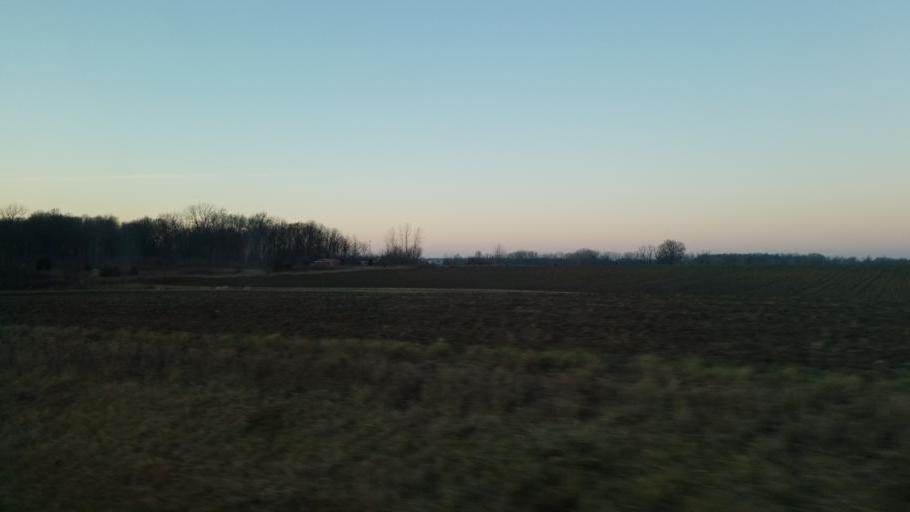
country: US
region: Ohio
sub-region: Crawford County
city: Bucyrus
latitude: 40.8265
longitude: -83.1062
